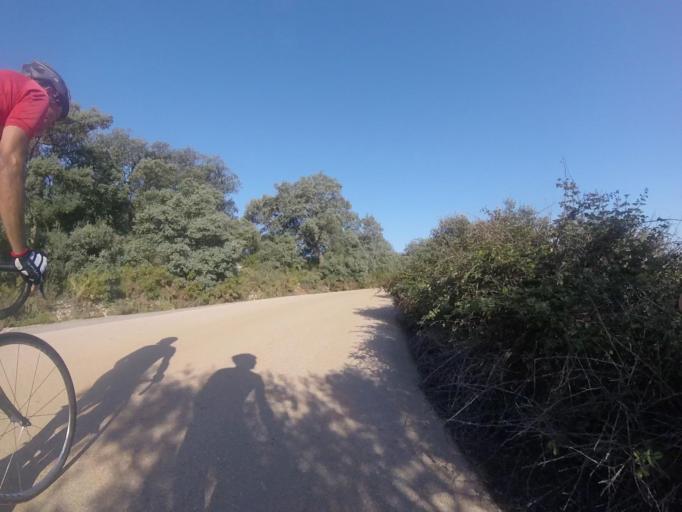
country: ES
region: Valencia
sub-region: Provincia de Castello
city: Benlloch
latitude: 40.2012
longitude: 0.0665
